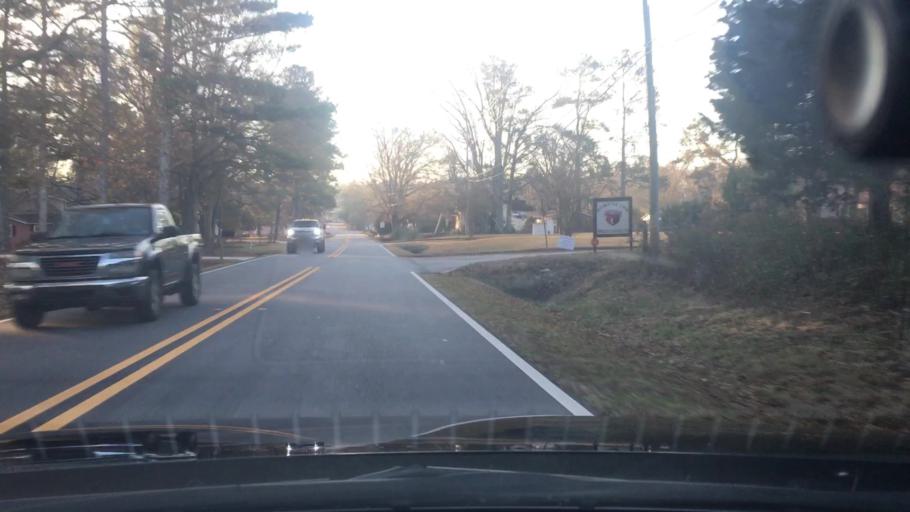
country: US
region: Georgia
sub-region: Coweta County
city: Senoia
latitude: 33.2945
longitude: -84.4603
